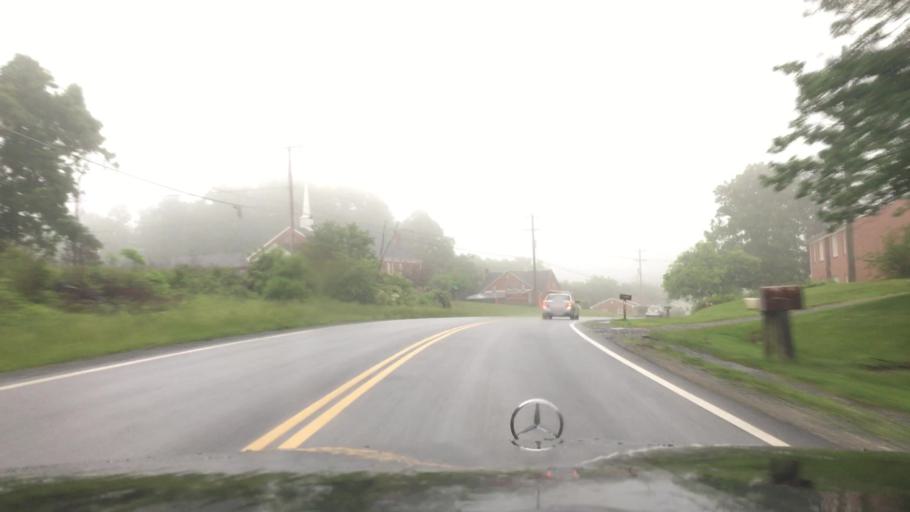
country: US
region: Virginia
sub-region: Campbell County
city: Timberlake
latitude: 37.3257
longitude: -79.2272
